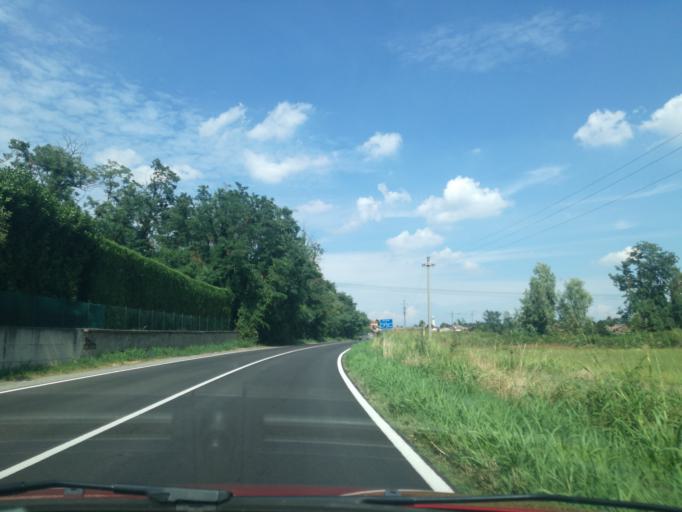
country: IT
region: Lombardy
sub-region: Citta metropolitana di Milano
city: Trezzano Rosa
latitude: 45.5773
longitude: 9.4753
